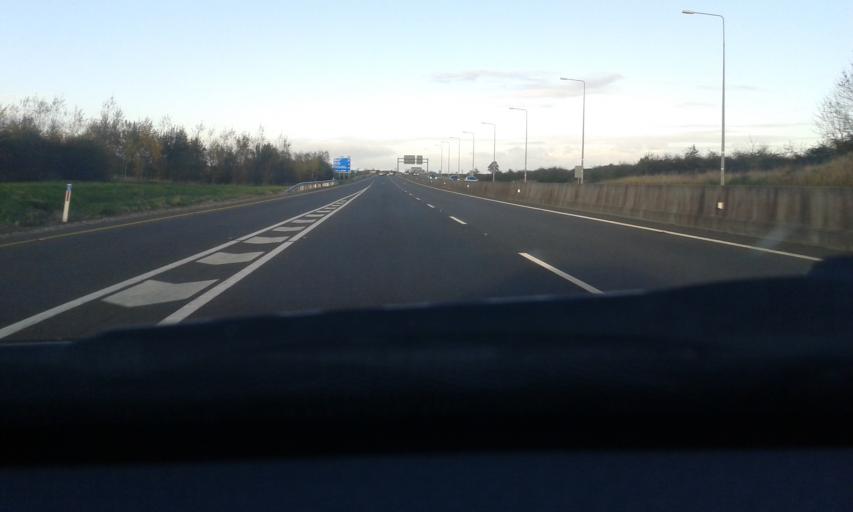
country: IE
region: Leinster
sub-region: Laois
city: Mountrath
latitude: 52.9269
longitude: -7.4750
